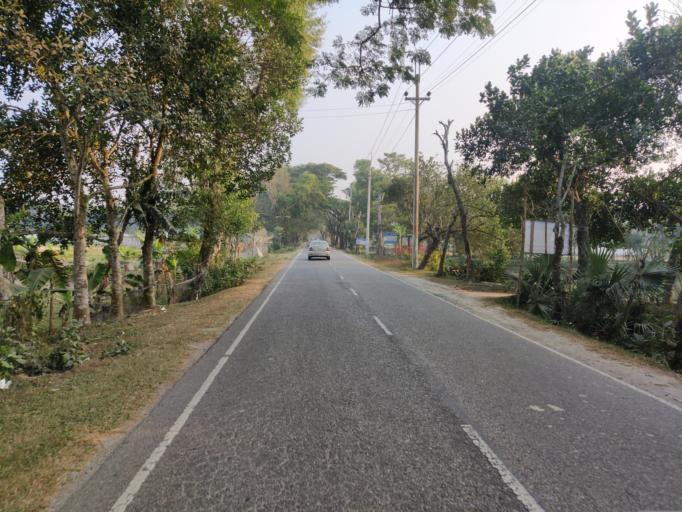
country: BD
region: Dhaka
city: Narsingdi
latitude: 24.0888
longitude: 90.7271
